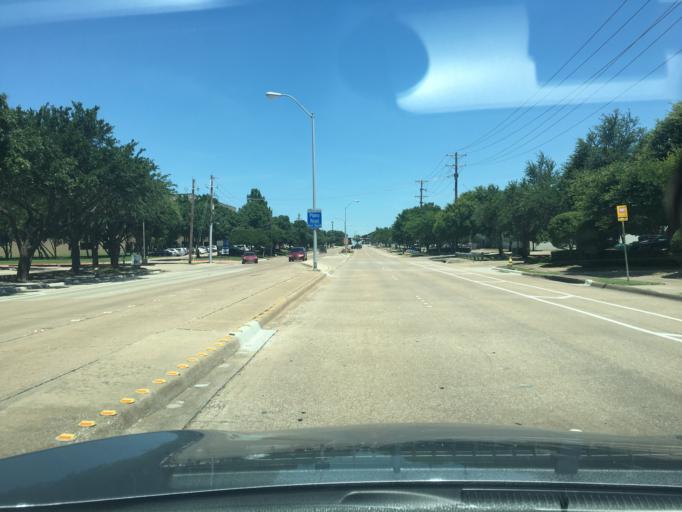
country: US
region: Texas
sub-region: Dallas County
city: Richardson
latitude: 32.9679
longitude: -96.7044
